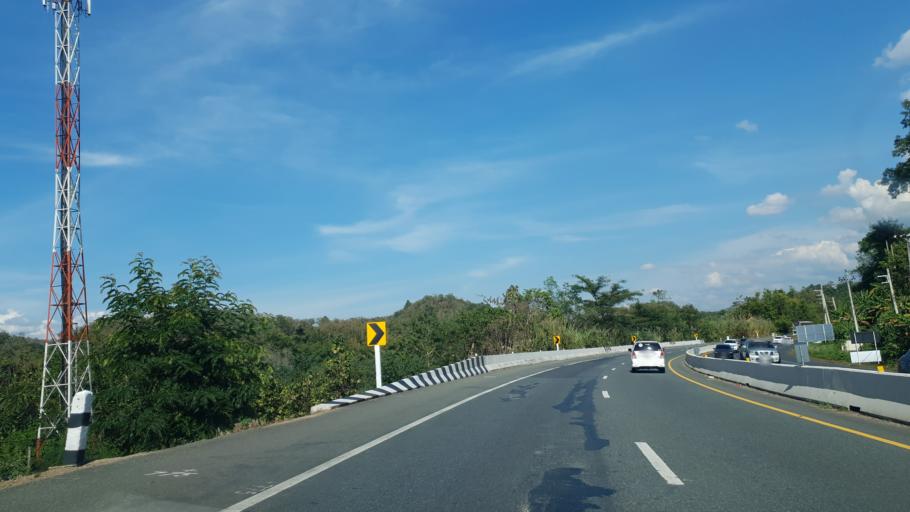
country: TH
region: Phrae
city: Den Chai
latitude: 17.8935
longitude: 100.0487
